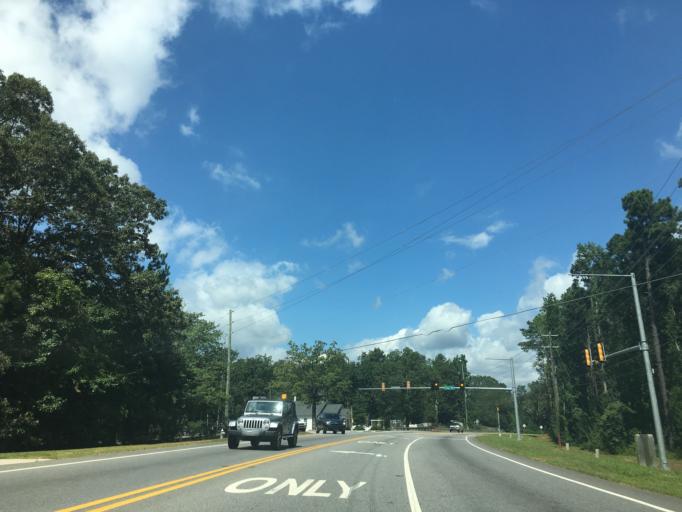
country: US
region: Georgia
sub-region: Fulton County
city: Roswell
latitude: 34.0951
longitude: -84.3663
